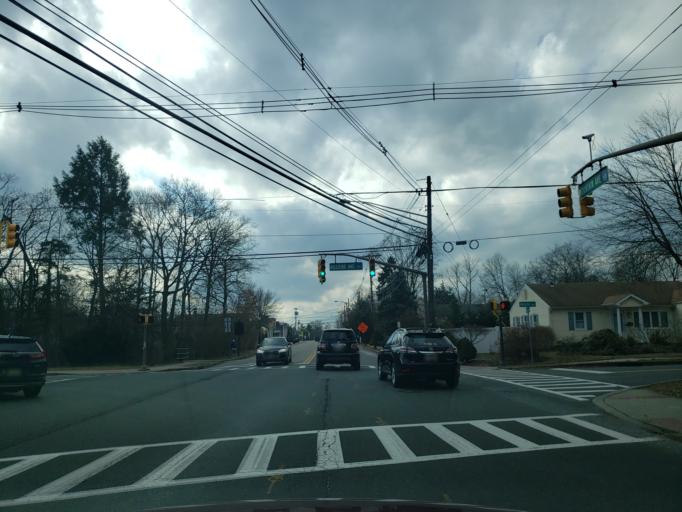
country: US
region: New Jersey
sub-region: Union County
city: Springfield
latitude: 40.6918
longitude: -74.3304
